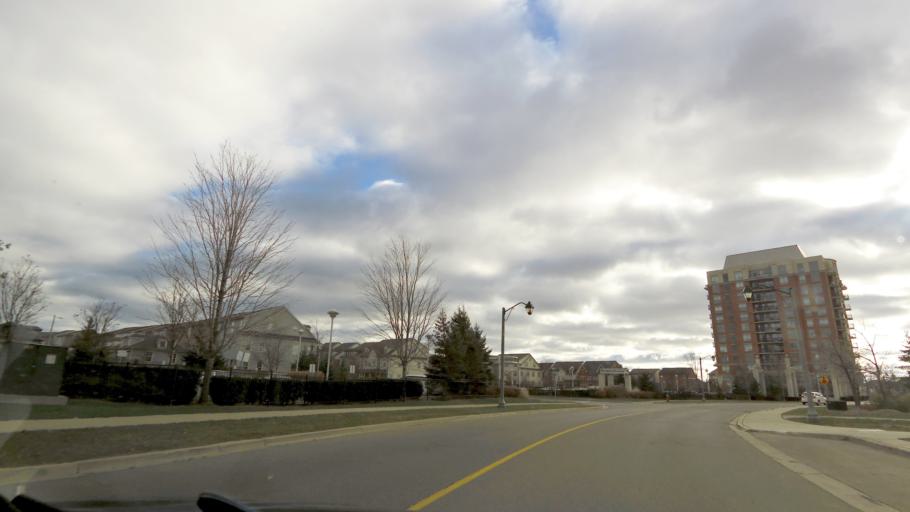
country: CA
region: Ontario
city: Oakville
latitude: 43.4792
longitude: -79.7220
